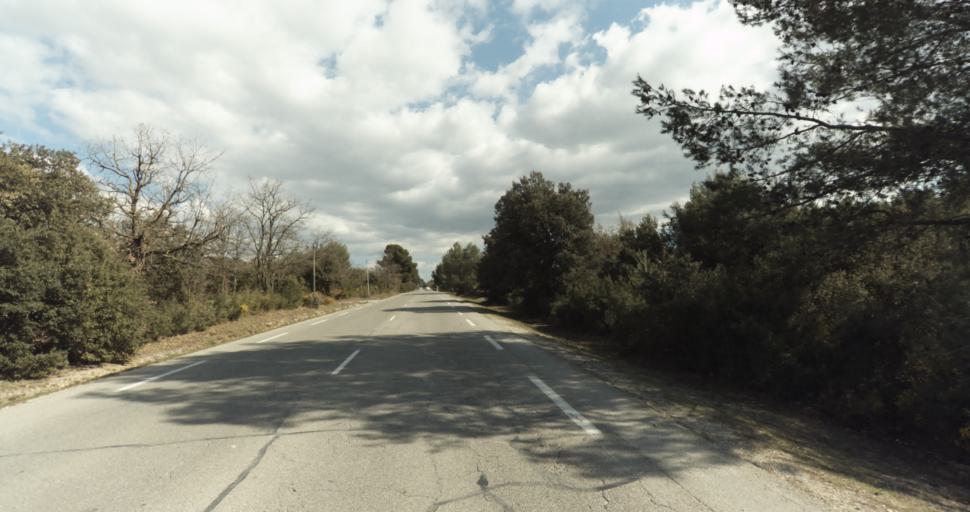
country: FR
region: Provence-Alpes-Cote d'Azur
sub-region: Departement des Bouches-du-Rhone
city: Greasque
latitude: 43.4472
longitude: 5.5139
